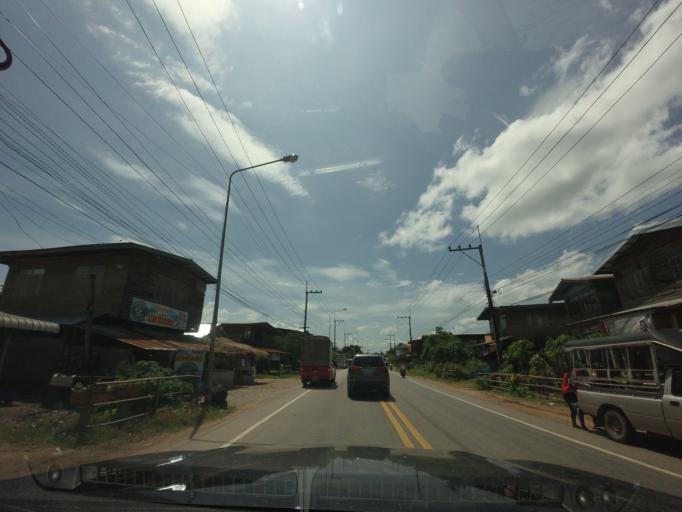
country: TH
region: Changwat Udon Thani
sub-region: Amphoe Ban Phue
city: Ban Phue
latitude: 17.7460
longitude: 102.3992
